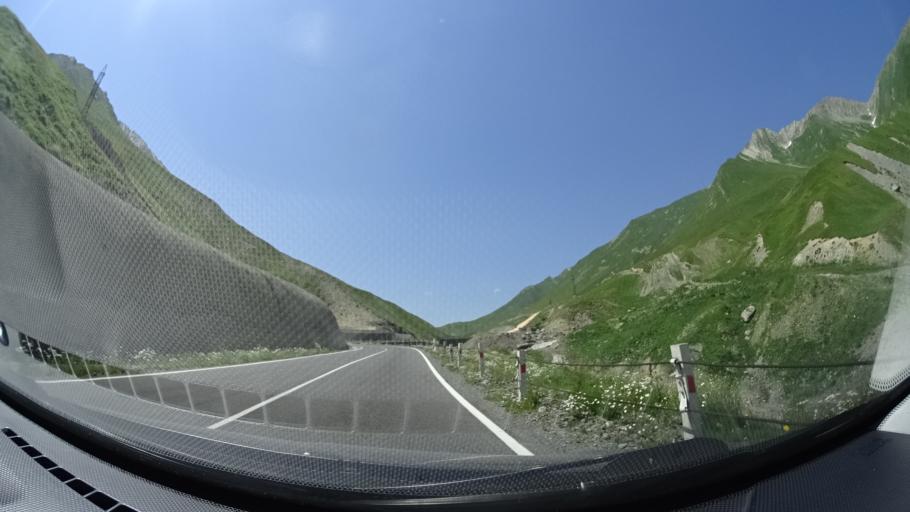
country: GE
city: Gudauri
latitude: 42.5364
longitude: 44.4768
